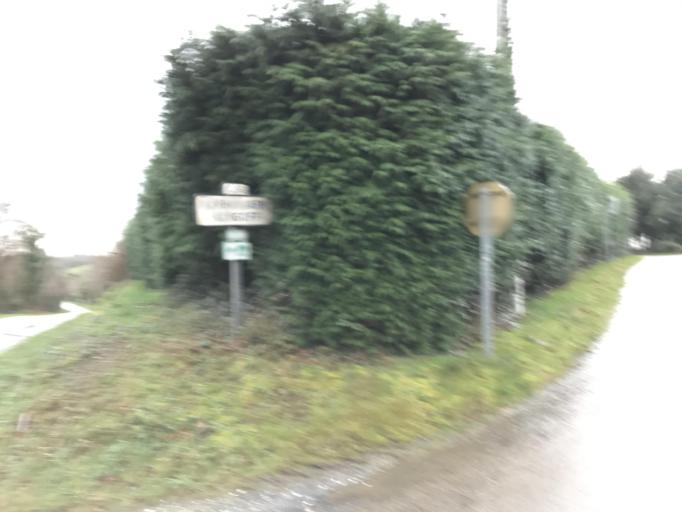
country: FR
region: Brittany
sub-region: Departement du Finistere
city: Loperhet
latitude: 48.3691
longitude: -4.3229
